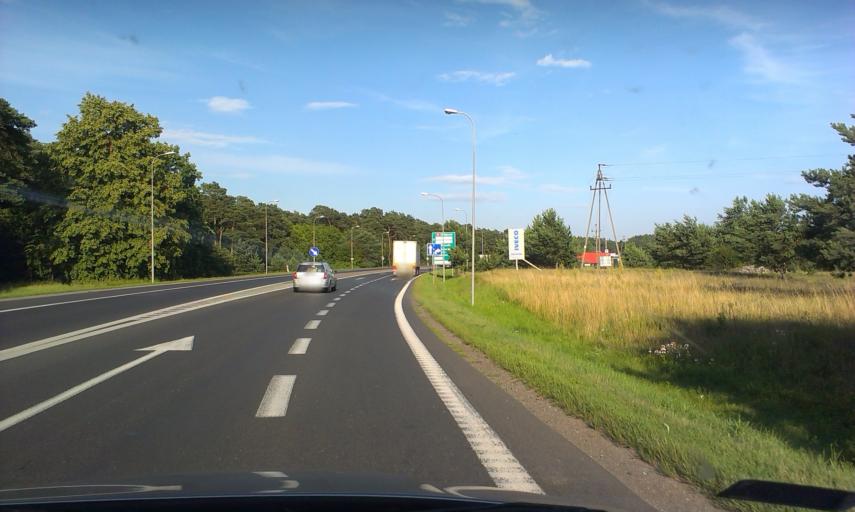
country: PL
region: Kujawsko-Pomorskie
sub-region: Powiat bydgoski
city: Biale Blota
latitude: 53.1573
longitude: 17.8857
